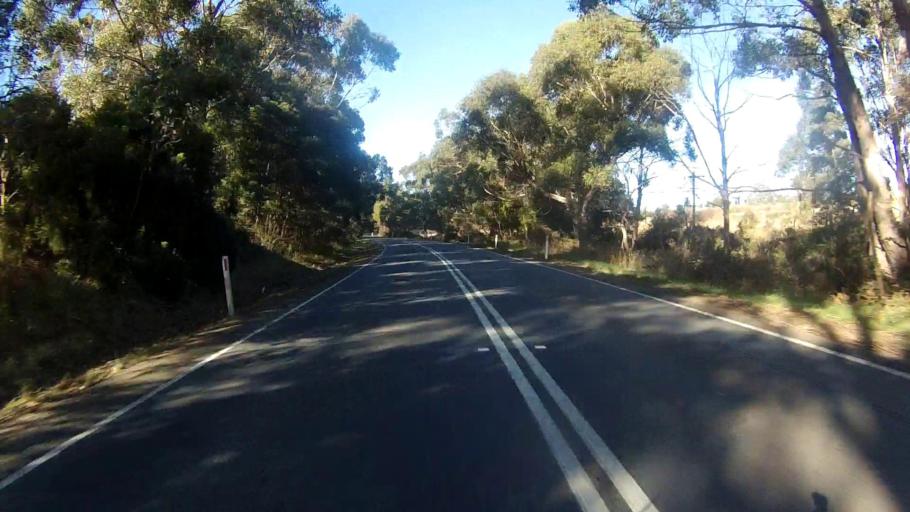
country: AU
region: Tasmania
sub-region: Sorell
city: Sorell
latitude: -42.8222
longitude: 147.8037
